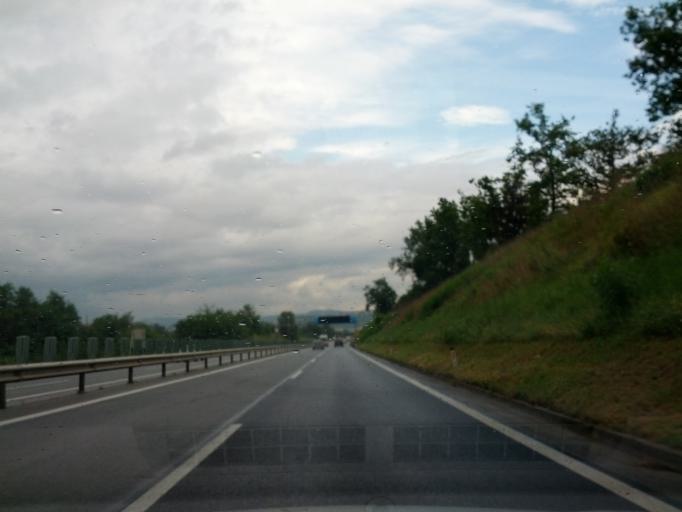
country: SI
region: Koper-Capodistria
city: Prade
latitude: 45.5437
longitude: 13.7556
